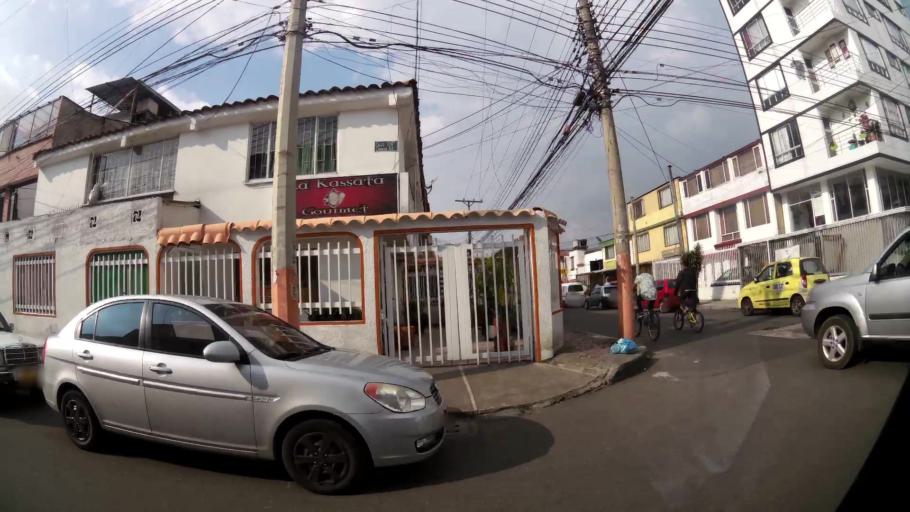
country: CO
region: Bogota D.C.
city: Barrio San Luis
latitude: 4.7223
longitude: -74.0576
